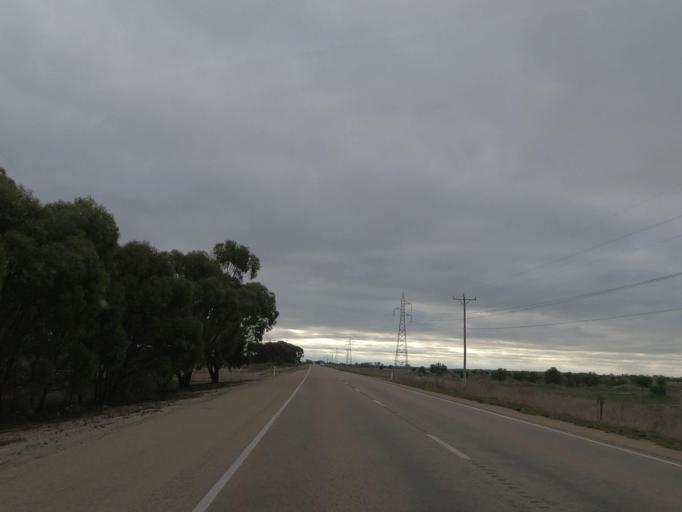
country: AU
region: Victoria
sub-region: Swan Hill
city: Swan Hill
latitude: -35.9038
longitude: 143.9470
